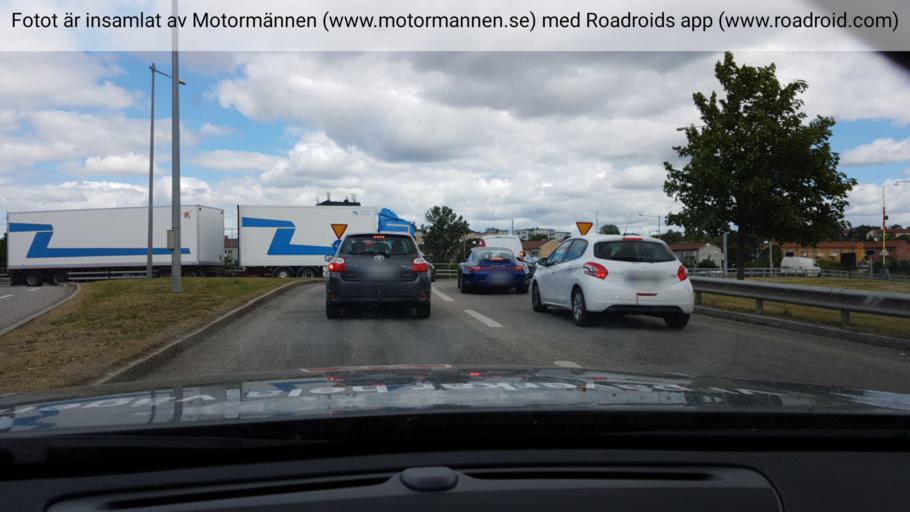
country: SE
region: Stockholm
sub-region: Stockholms Kommun
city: Arsta
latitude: 59.2953
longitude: 18.0354
